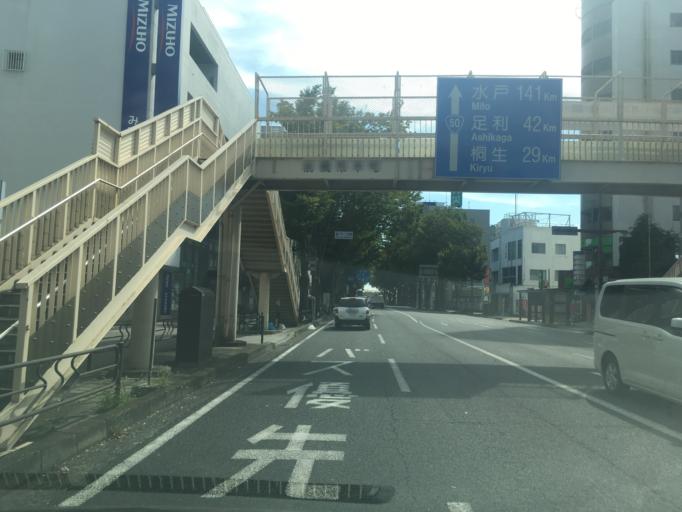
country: JP
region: Gunma
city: Maebashi-shi
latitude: 36.3905
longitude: 139.0690
